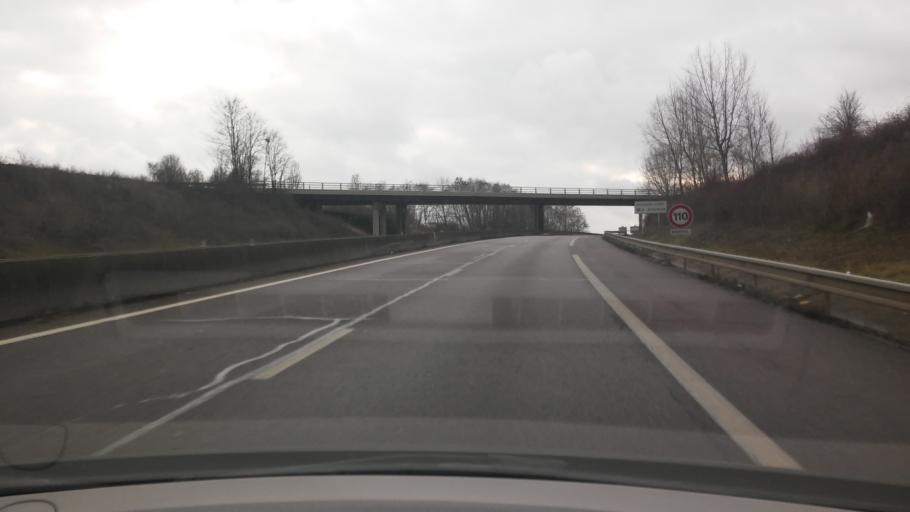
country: FR
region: Lorraine
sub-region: Departement de la Moselle
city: Saint-Julien-les-Metz
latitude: 49.1267
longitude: 6.2402
